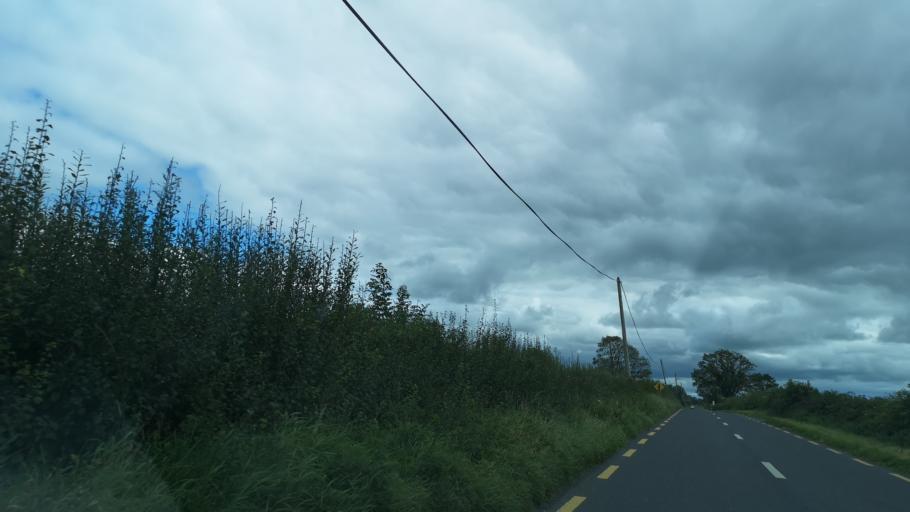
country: IE
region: Leinster
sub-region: Uibh Fhaili
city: Banagher
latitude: 53.2656
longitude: -7.9976
